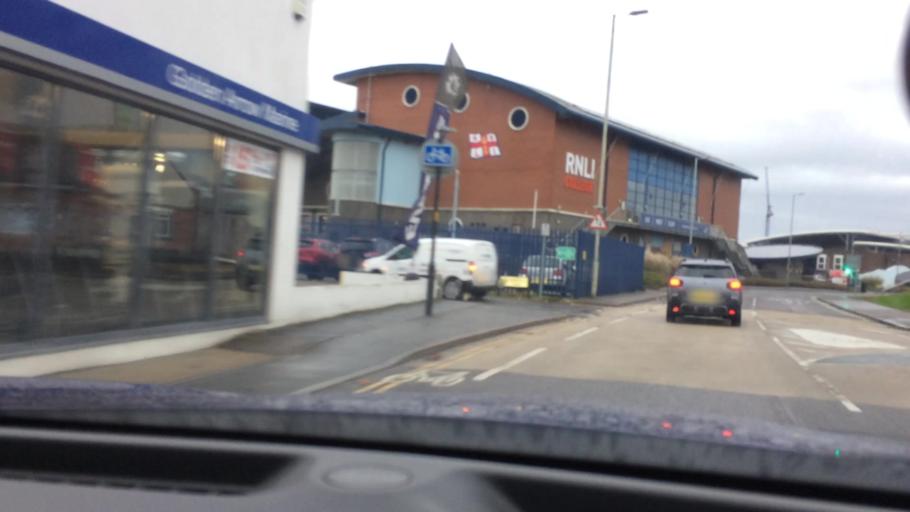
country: GB
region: England
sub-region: Poole
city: Poole
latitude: 50.7163
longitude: -1.9897
